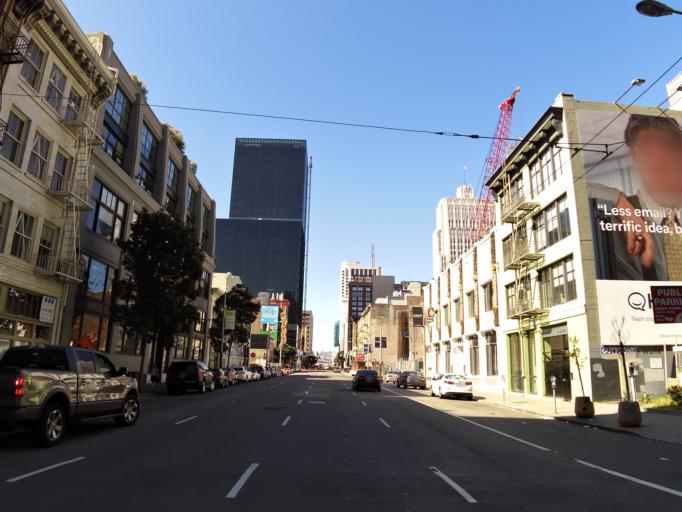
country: US
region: California
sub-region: San Francisco County
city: San Francisco
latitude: 37.7881
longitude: -122.3967
